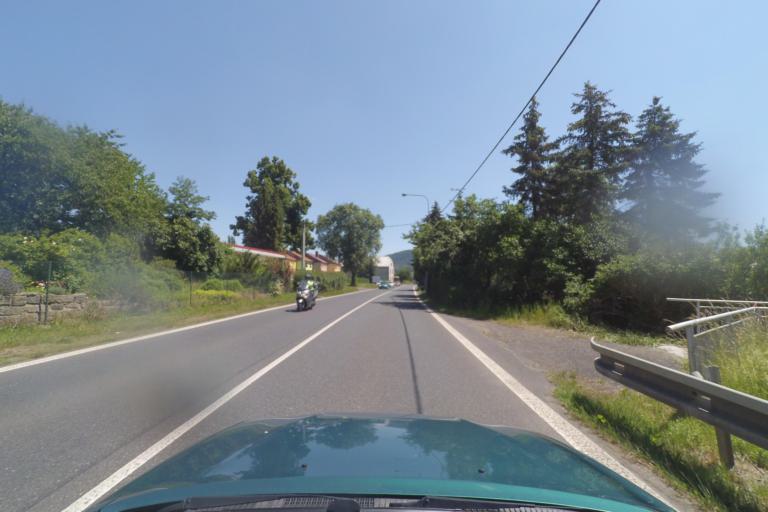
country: CZ
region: Ustecky
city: Libouchec
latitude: 50.7609
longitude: 14.0577
